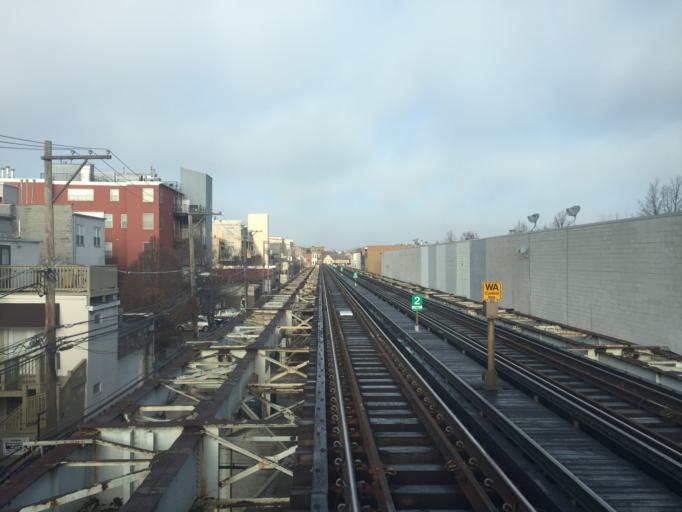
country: US
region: Illinois
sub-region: Cook County
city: Chicago
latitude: 41.9119
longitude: -87.6501
